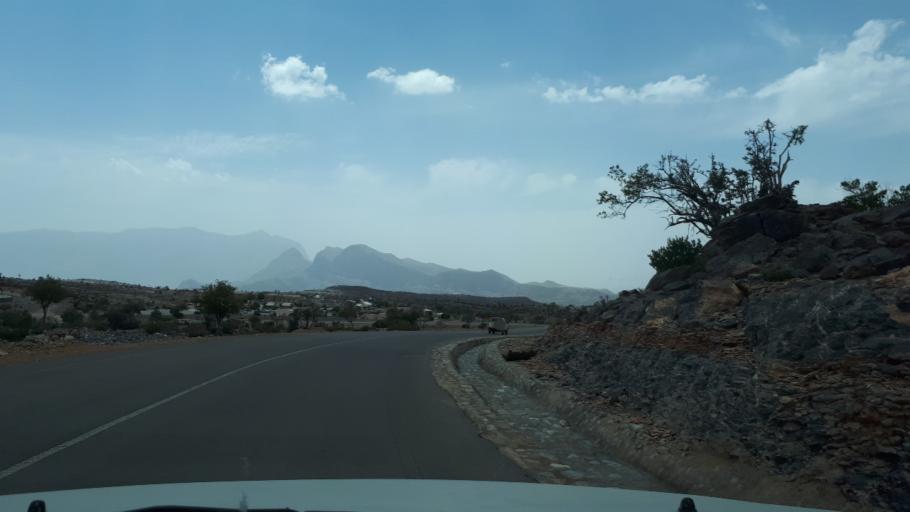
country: OM
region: Muhafazat ad Dakhiliyah
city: Bahla'
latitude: 23.2092
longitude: 57.2017
